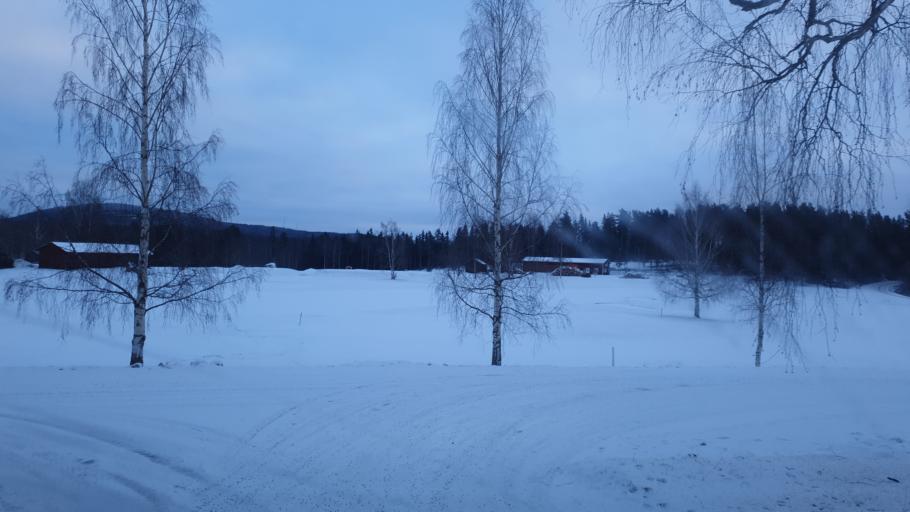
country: SE
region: Gaevleborg
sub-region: Bollnas Kommun
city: Kilafors
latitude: 61.2571
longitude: 16.5374
